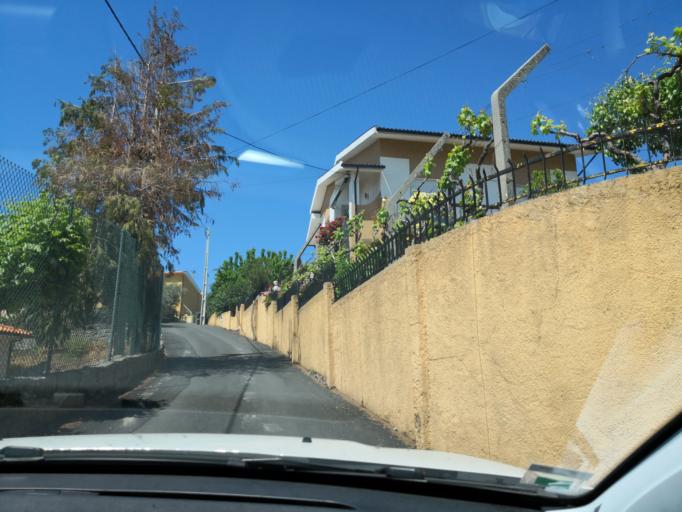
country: PT
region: Vila Real
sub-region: Santa Marta de Penaguiao
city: Santa Marta de Penaguiao
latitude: 41.2275
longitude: -7.7293
